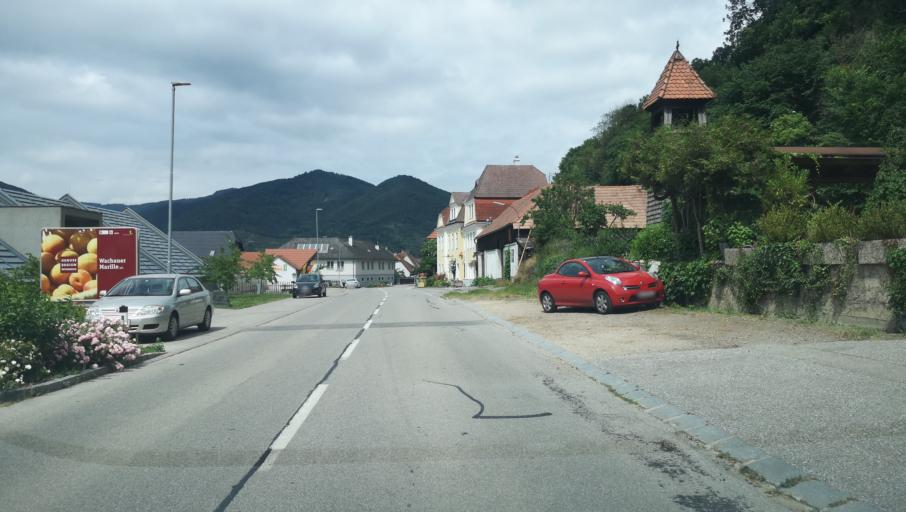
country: AT
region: Lower Austria
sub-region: Politischer Bezirk Krems
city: Spitz
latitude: 48.3522
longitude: 15.4137
